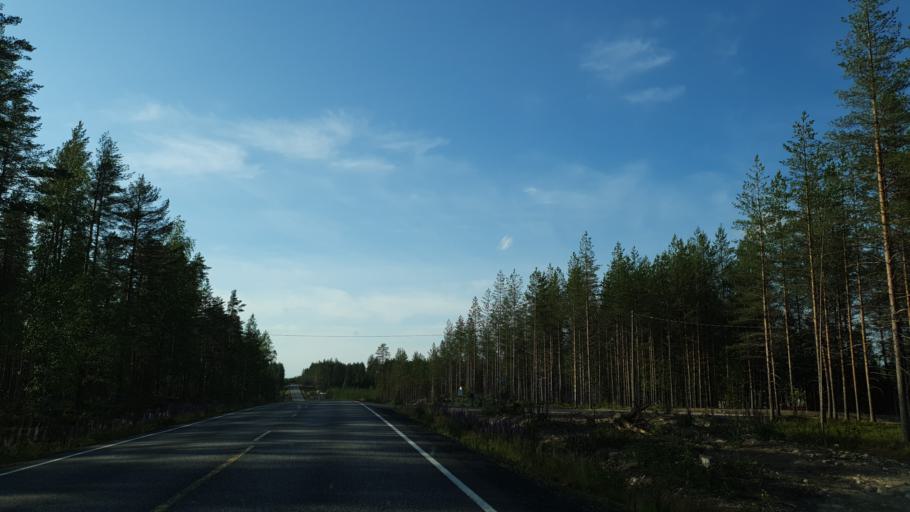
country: FI
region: Kainuu
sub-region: Kehys-Kainuu
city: Kuhmo
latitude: 64.0909
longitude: 29.4808
